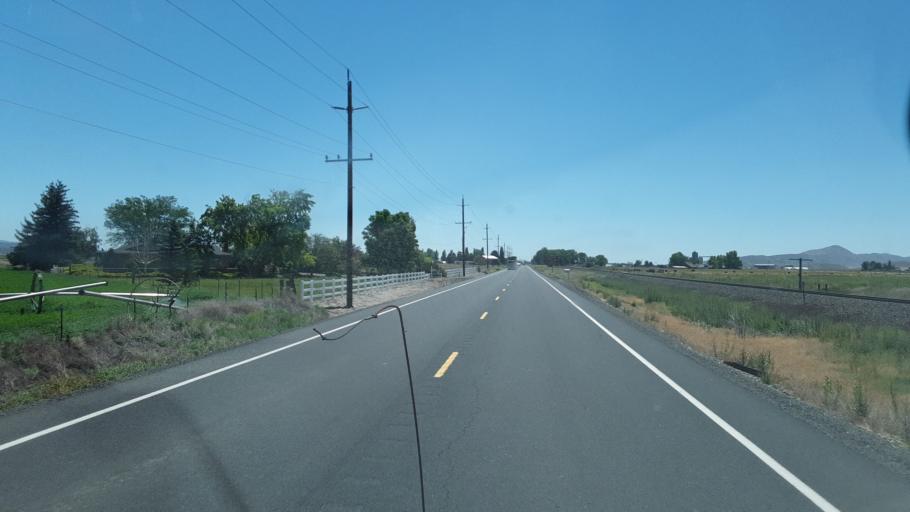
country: US
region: California
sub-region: Siskiyou County
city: Tulelake
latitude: 42.0496
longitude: -121.6365
